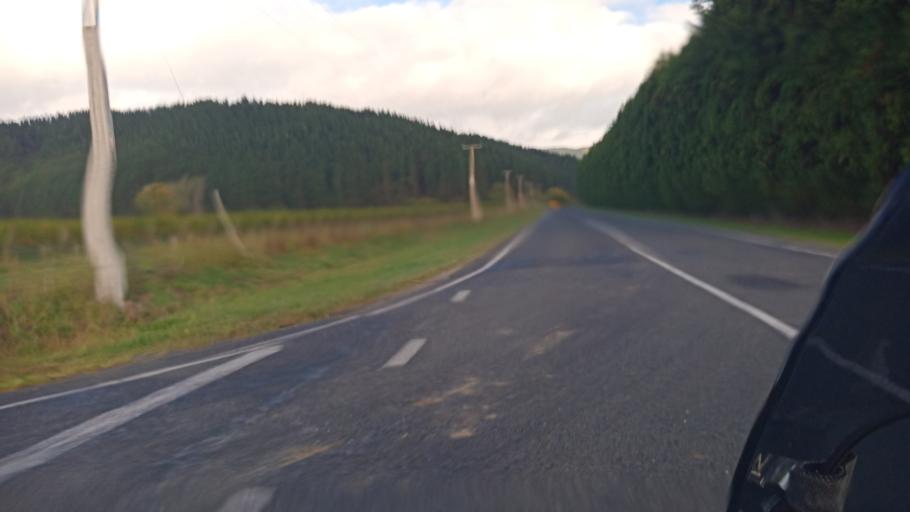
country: NZ
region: Gisborne
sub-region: Gisborne District
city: Gisborne
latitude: -38.6346
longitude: 177.8570
